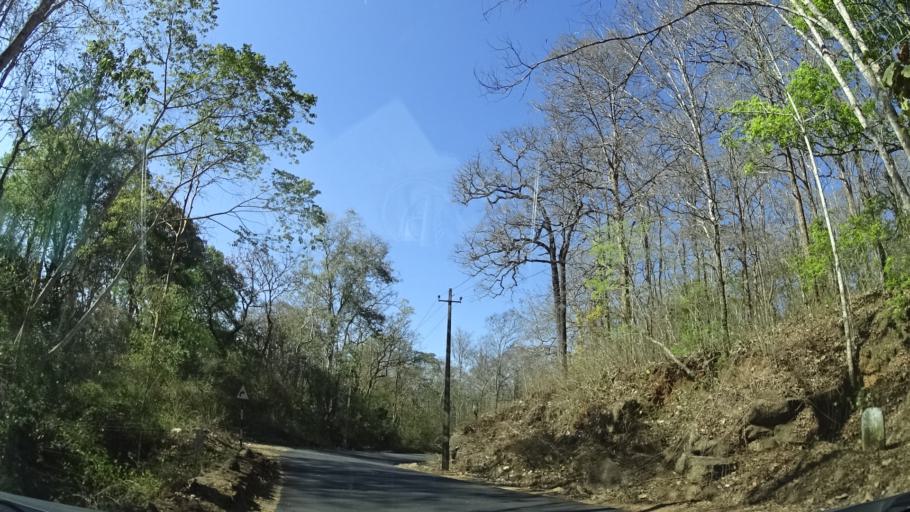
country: IN
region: Karnataka
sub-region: Chikmagalur
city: Koppa
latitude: 13.3537
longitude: 75.4927
